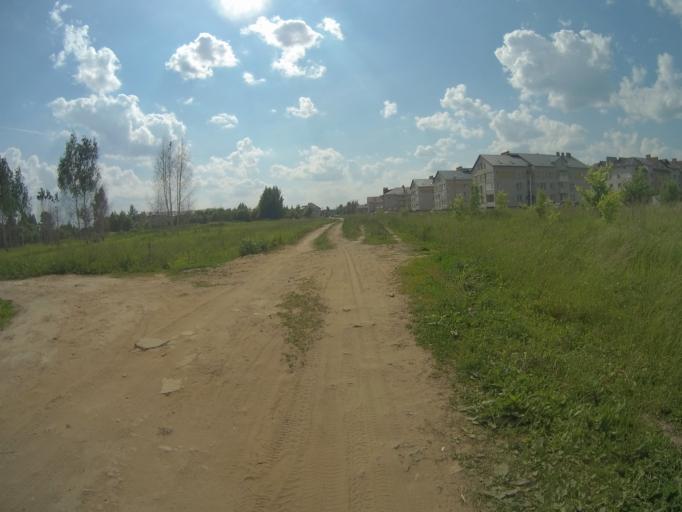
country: RU
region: Vladimir
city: Suzdal'
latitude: 56.4347
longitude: 40.4579
